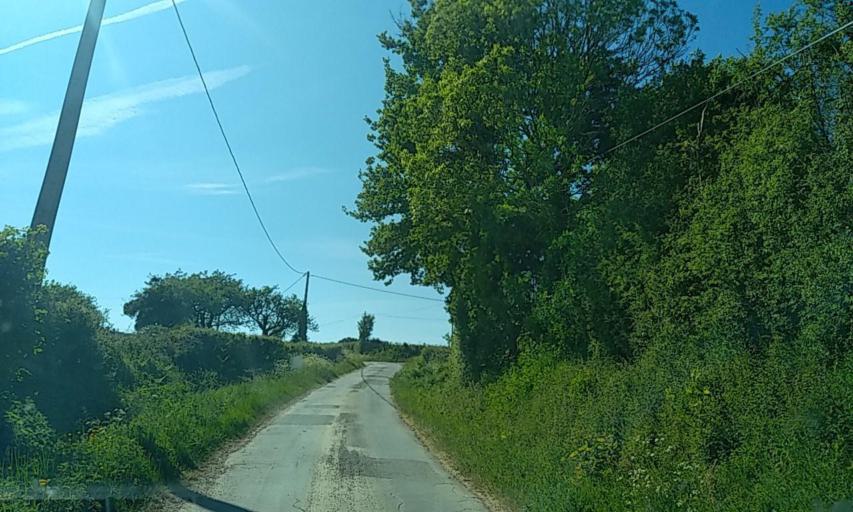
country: FR
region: Poitou-Charentes
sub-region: Departement des Deux-Sevres
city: Boisme
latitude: 46.7770
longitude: -0.4065
